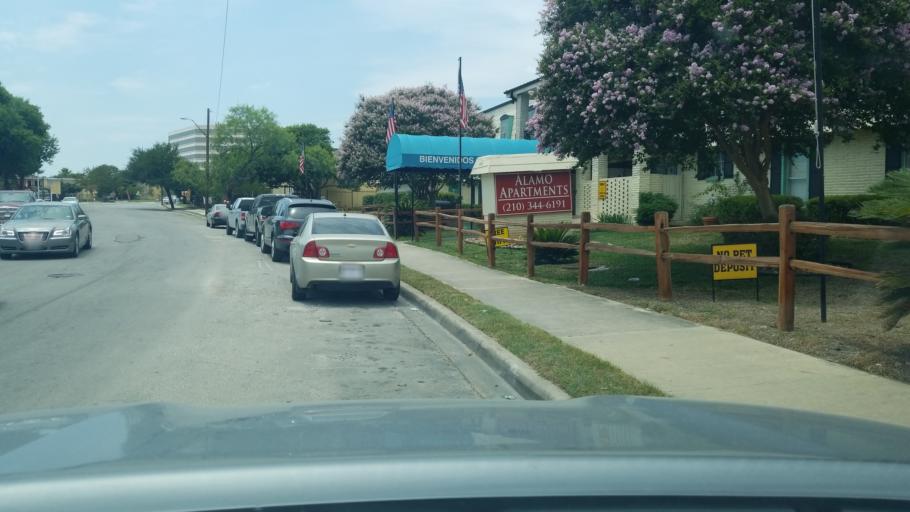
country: US
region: Texas
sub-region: Bexar County
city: Castle Hills
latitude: 29.5314
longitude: -98.4913
